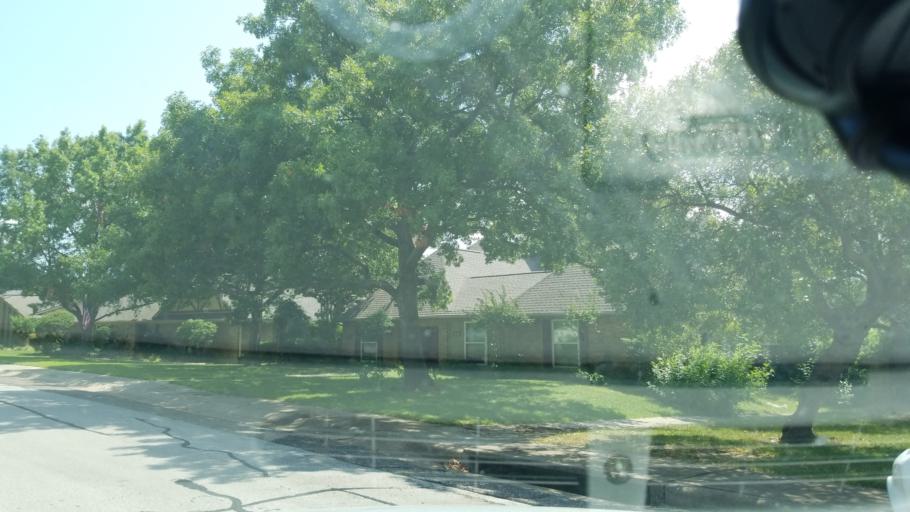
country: US
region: Texas
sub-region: Dallas County
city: Carrollton
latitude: 32.9642
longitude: -96.8626
